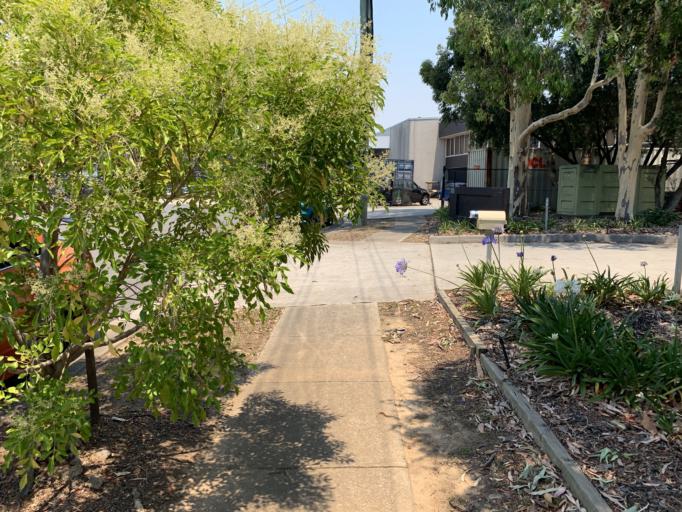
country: AU
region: New South Wales
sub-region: Holroyd
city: Girraween
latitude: -33.7743
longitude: 150.9529
